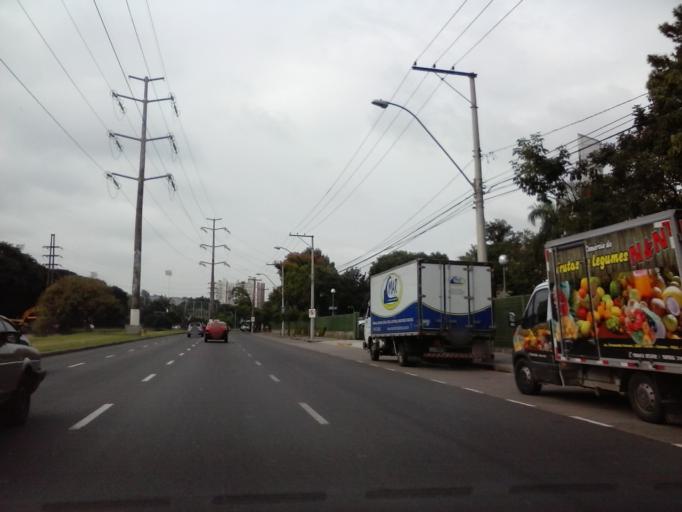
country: BR
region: Rio Grande do Sul
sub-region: Porto Alegre
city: Porto Alegre
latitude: -30.0567
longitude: -51.1734
